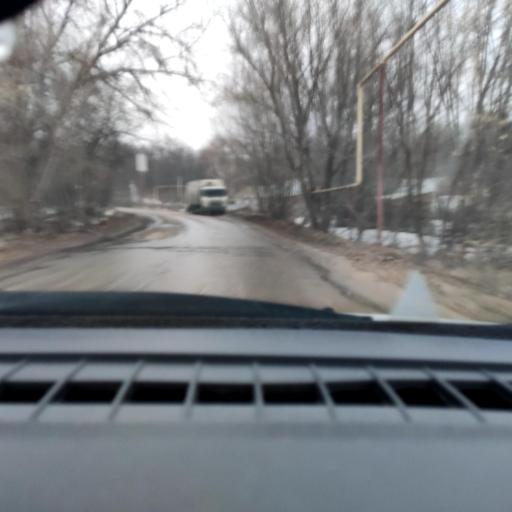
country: RU
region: Samara
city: Novosemeykino
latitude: 53.3342
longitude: 50.2706
